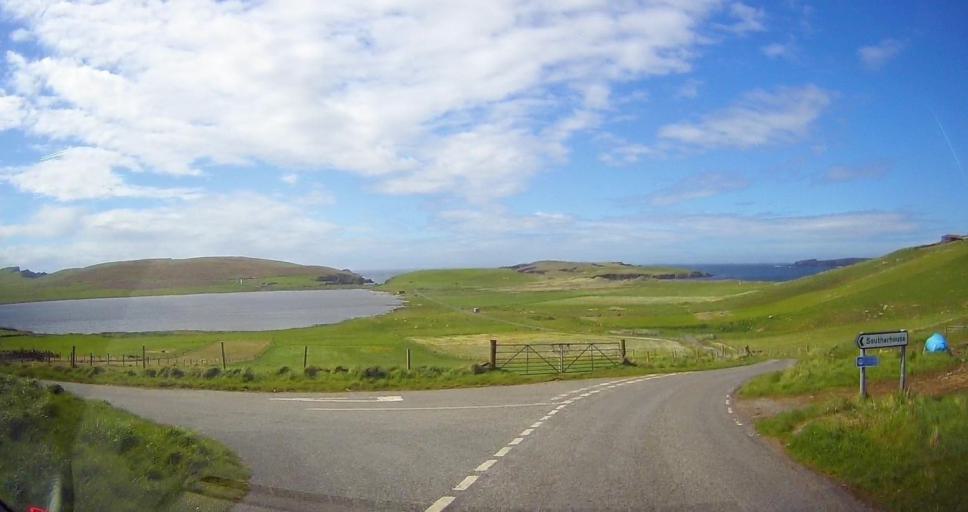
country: GB
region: Scotland
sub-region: Shetland Islands
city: Sandwick
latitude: 59.9400
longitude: -1.3258
